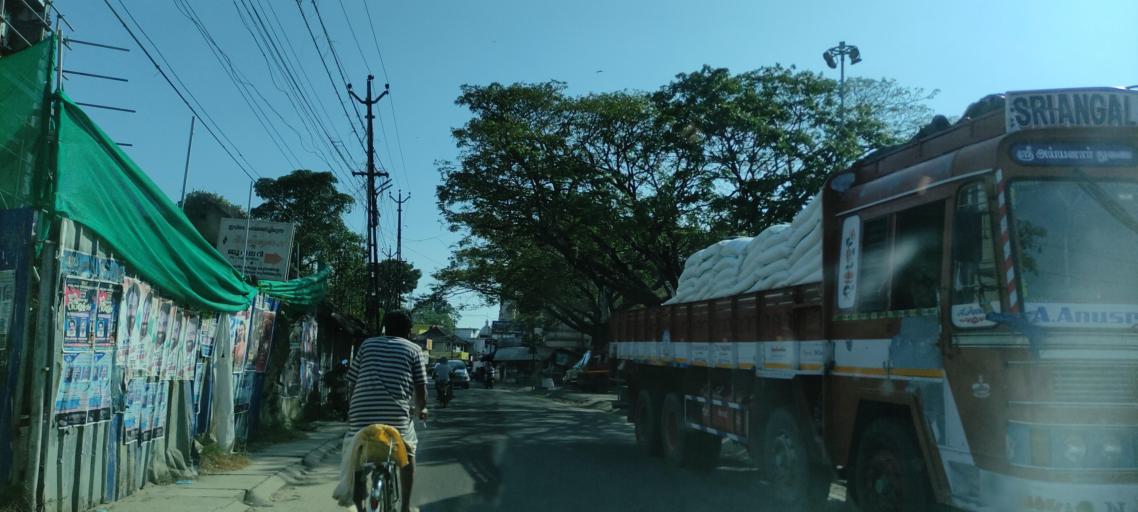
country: IN
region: Kerala
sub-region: Alappuzha
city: Vayalar
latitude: 9.6897
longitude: 76.3369
